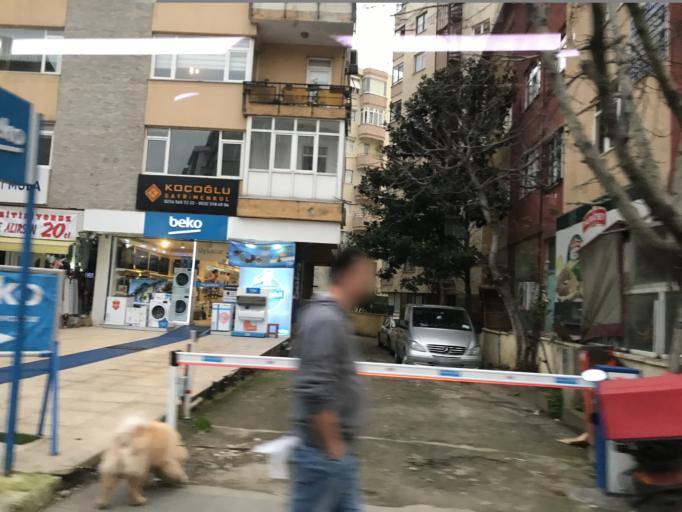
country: TR
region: Istanbul
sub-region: Atasehir
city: Atasehir
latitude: 40.9826
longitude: 29.0656
